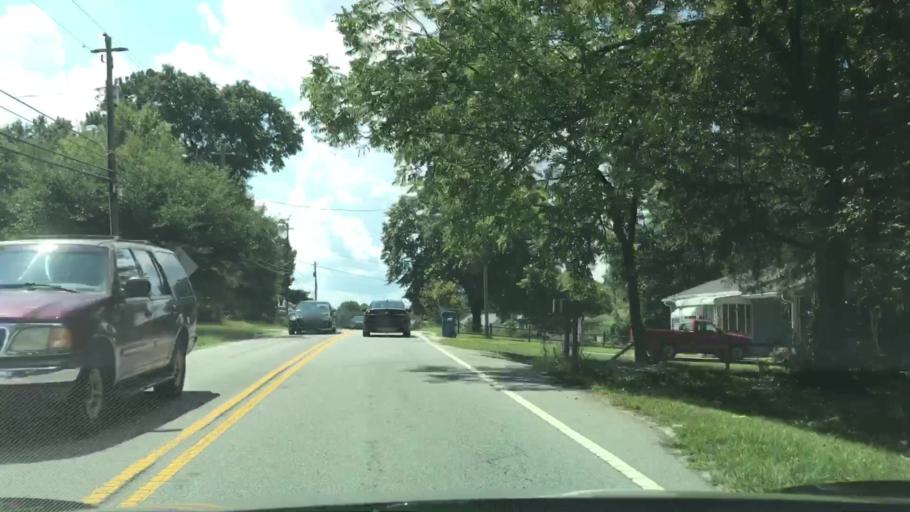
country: US
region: Georgia
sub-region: Gwinnett County
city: Snellville
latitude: 33.9241
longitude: -84.0626
